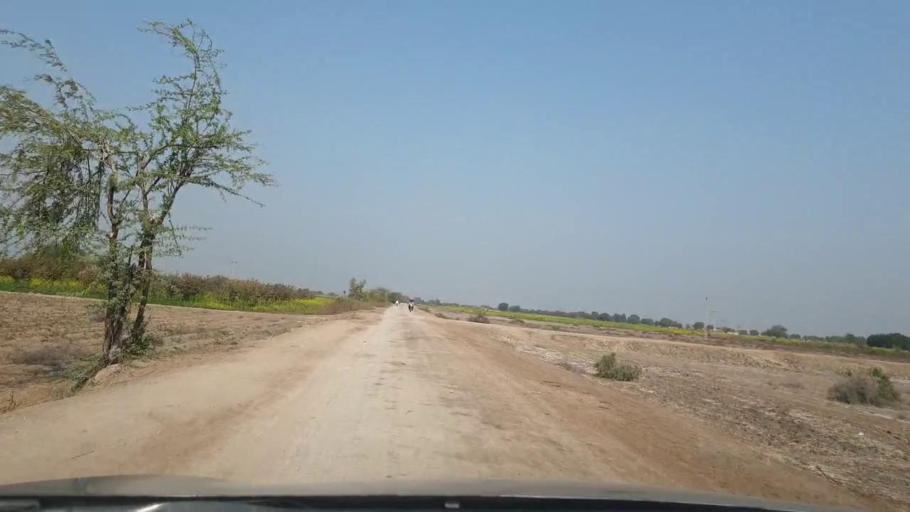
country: PK
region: Sindh
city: Tando Allahyar
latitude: 25.5434
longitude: 68.8141
